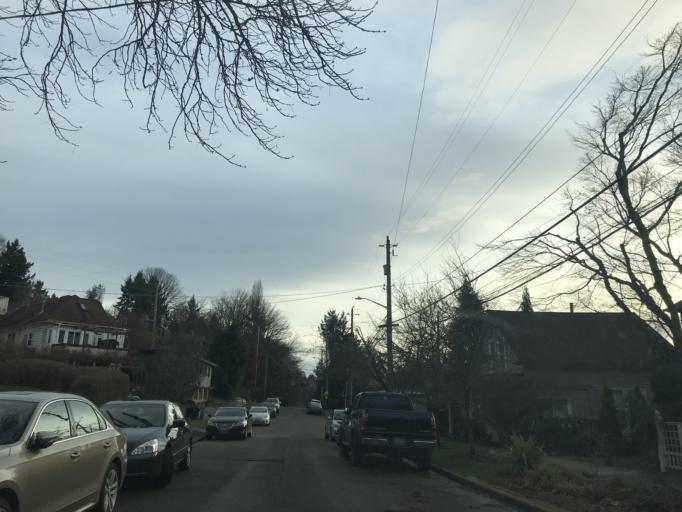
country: US
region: Washington
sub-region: King County
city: Seattle
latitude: 47.6281
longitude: -122.2909
